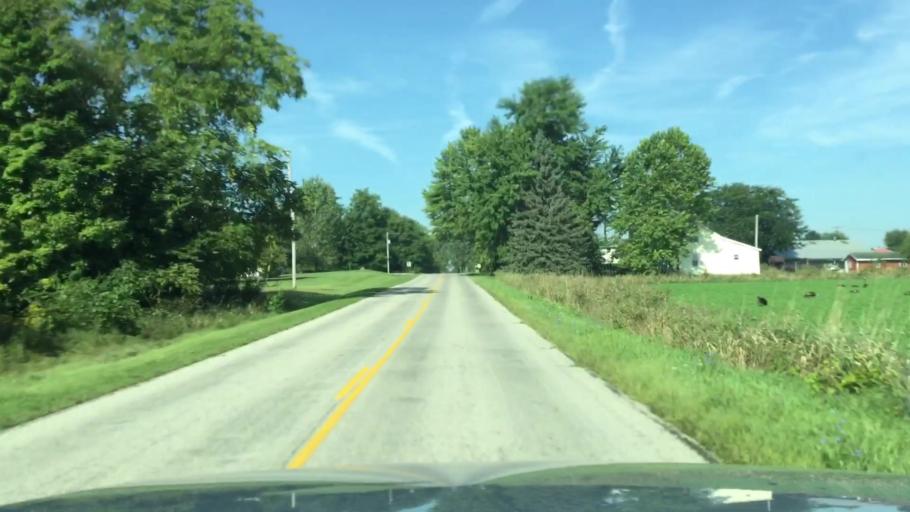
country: US
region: Michigan
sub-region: Lenawee County
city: Manitou Beach-Devils Lake
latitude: 41.9425
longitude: -84.3574
